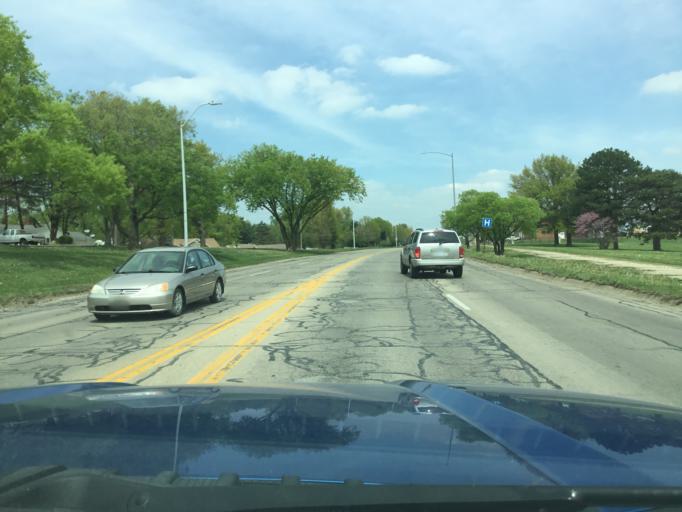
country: US
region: Kansas
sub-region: Shawnee County
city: Topeka
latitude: 39.0164
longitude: -95.6874
